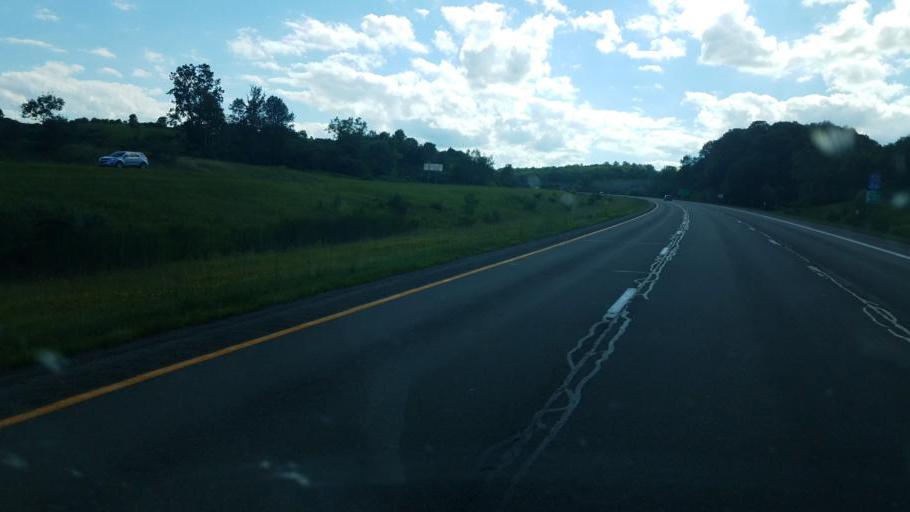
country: US
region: New York
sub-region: Steuben County
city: Hornell
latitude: 42.3668
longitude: -77.6915
